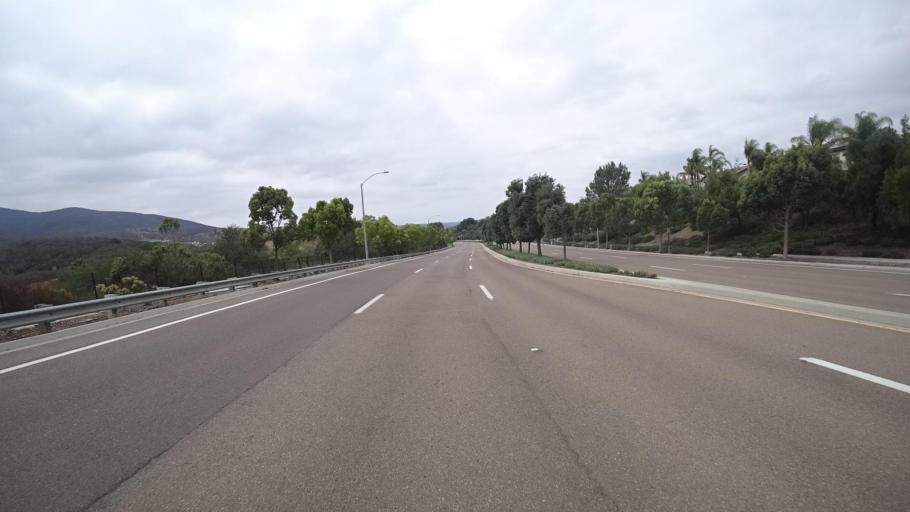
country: US
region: California
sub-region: San Diego County
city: Poway
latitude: 33.0022
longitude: -117.1014
